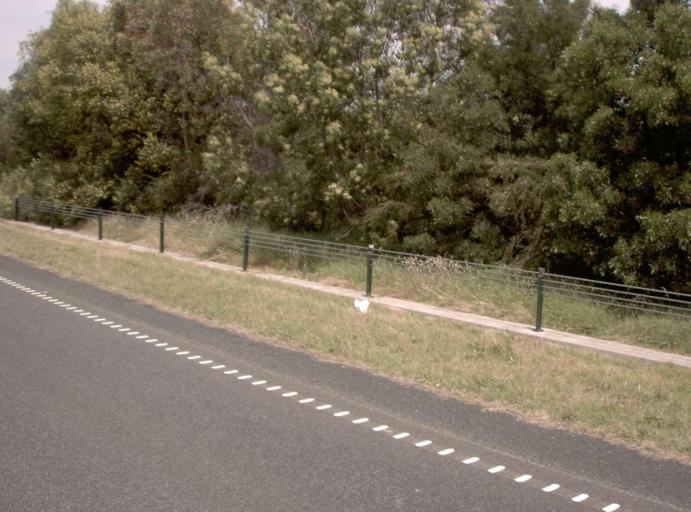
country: AU
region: Victoria
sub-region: Kingston
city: Patterson Lakes
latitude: -38.0768
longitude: 145.1500
